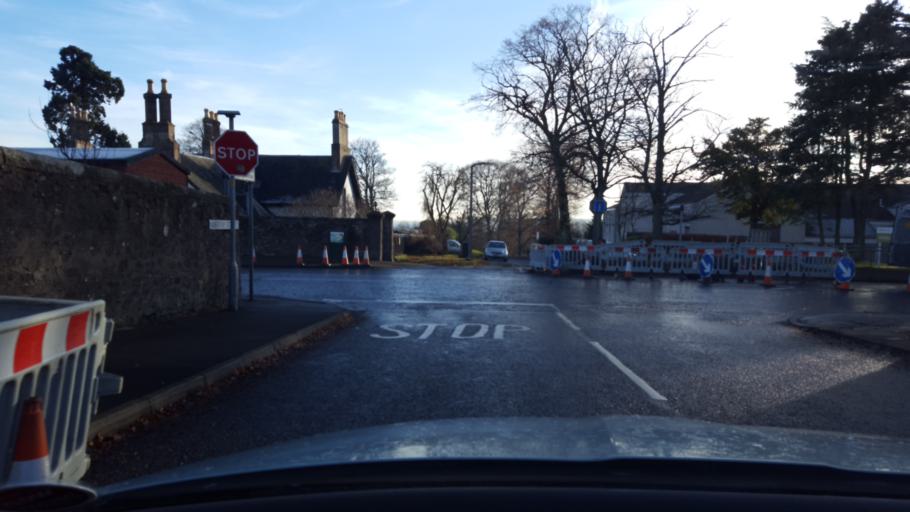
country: GB
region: Scotland
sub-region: Fife
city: Tayport
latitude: 56.4711
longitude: -2.8526
